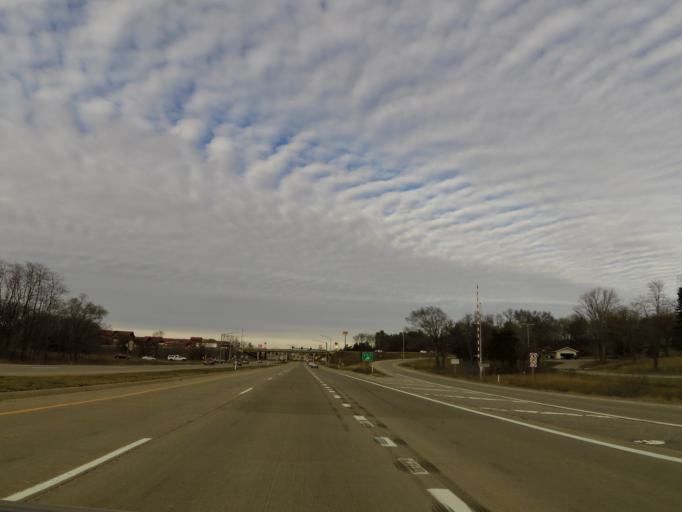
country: US
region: Wisconsin
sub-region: Sauk County
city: Lake Delton
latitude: 43.5668
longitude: -89.7783
